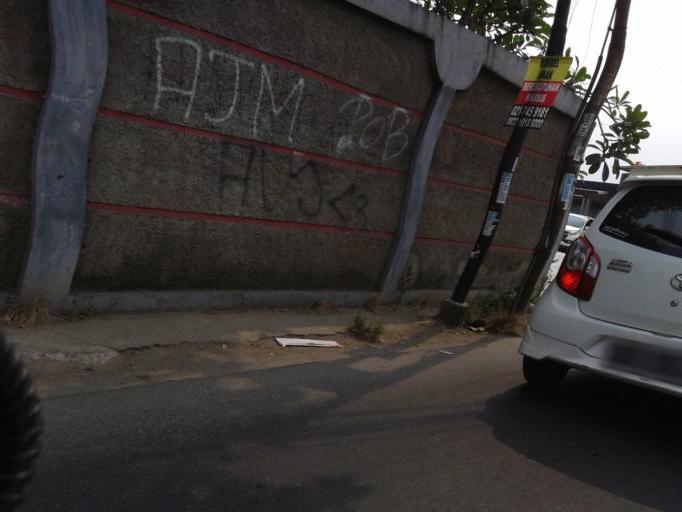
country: ID
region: Banten
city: South Tangerang
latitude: -6.2914
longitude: 106.7313
